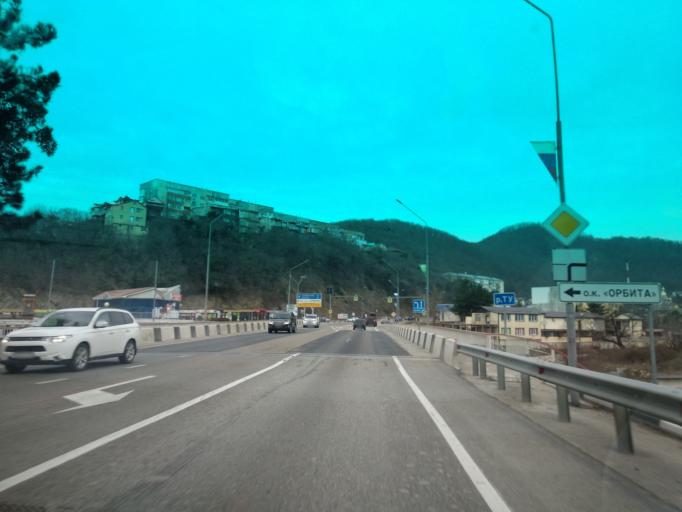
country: RU
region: Krasnodarskiy
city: Ol'ginka
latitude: 44.1987
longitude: 38.8892
